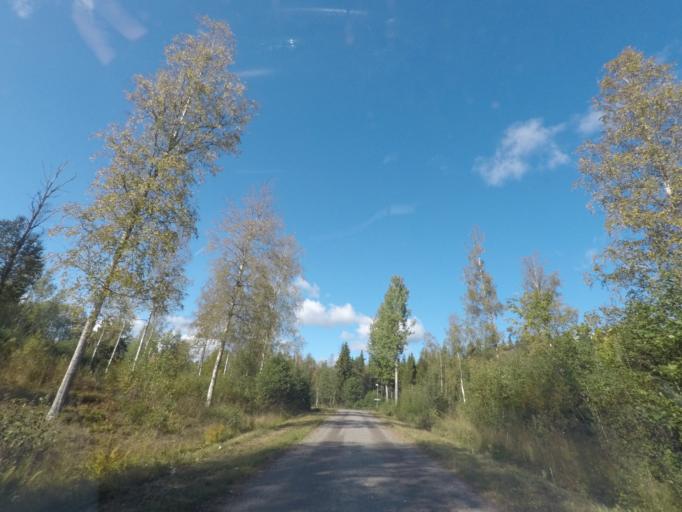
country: SE
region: Vaestmanland
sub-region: Skinnskattebergs Kommun
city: Skinnskatteberg
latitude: 59.8303
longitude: 15.5208
